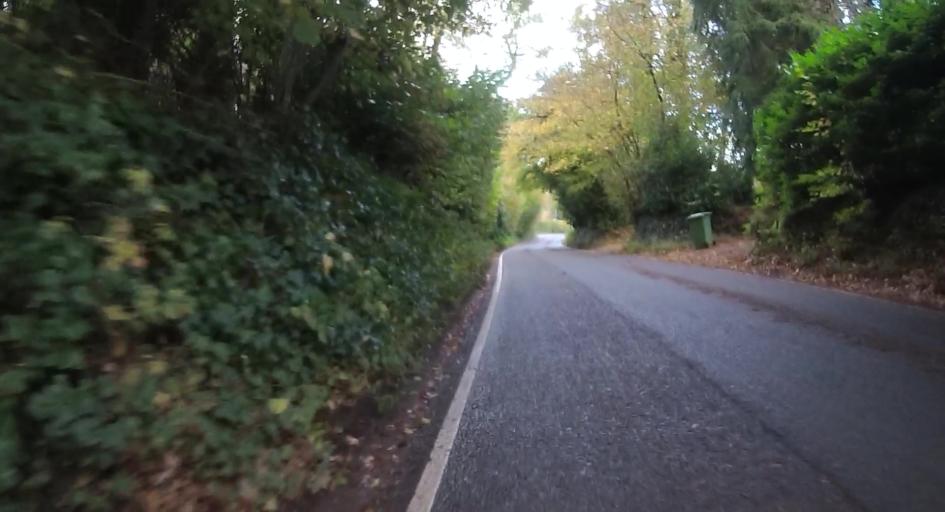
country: GB
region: England
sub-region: Hampshire
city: Alton
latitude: 51.1432
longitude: -1.0107
